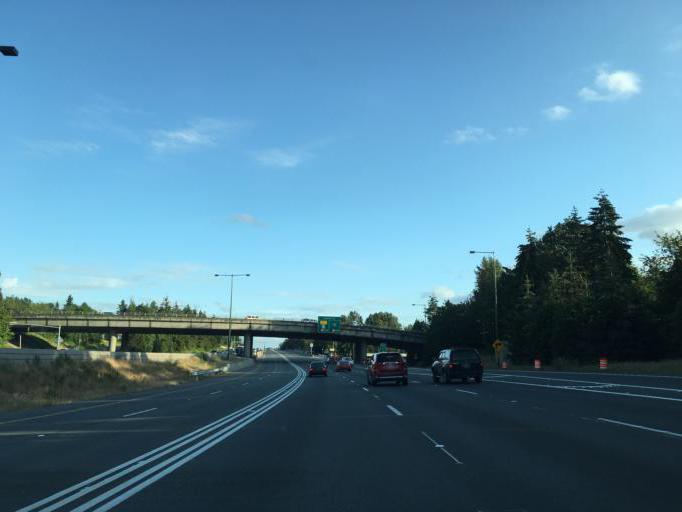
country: US
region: Washington
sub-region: King County
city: Kirkland
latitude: 47.6712
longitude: -122.1871
